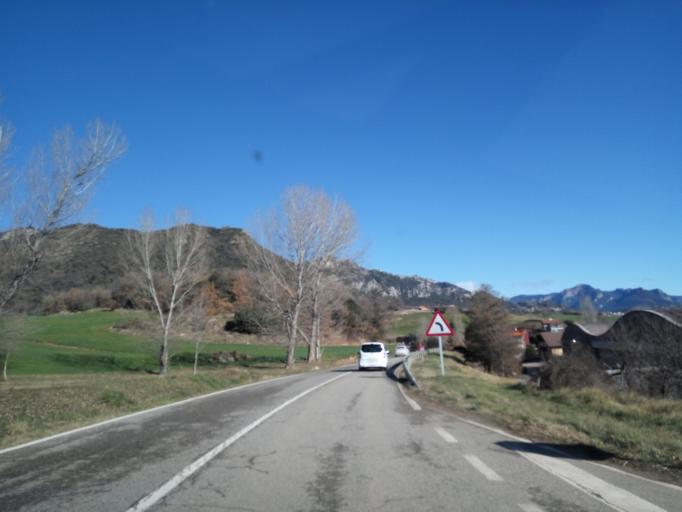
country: ES
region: Catalonia
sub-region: Provincia de Barcelona
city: Avia
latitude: 42.0776
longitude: 1.8134
